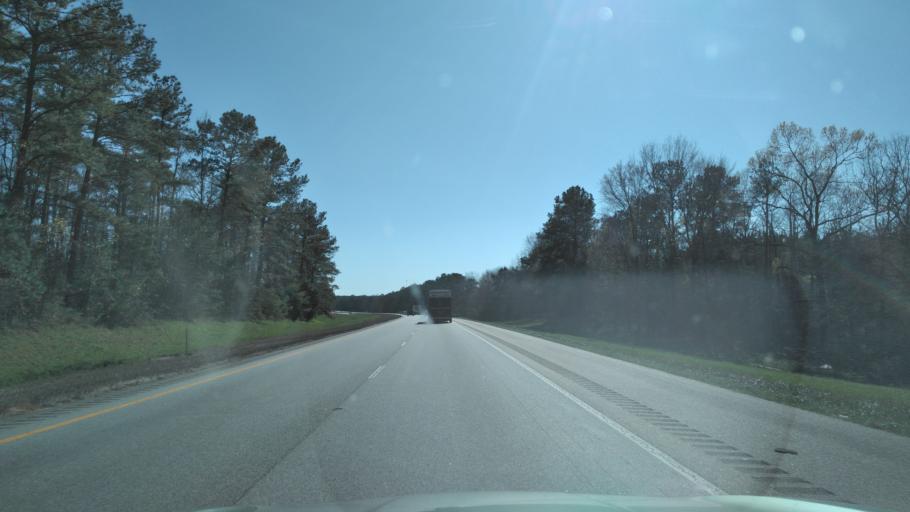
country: US
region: Alabama
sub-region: Lowndes County
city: Fort Deposit
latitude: 32.0487
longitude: -86.5023
